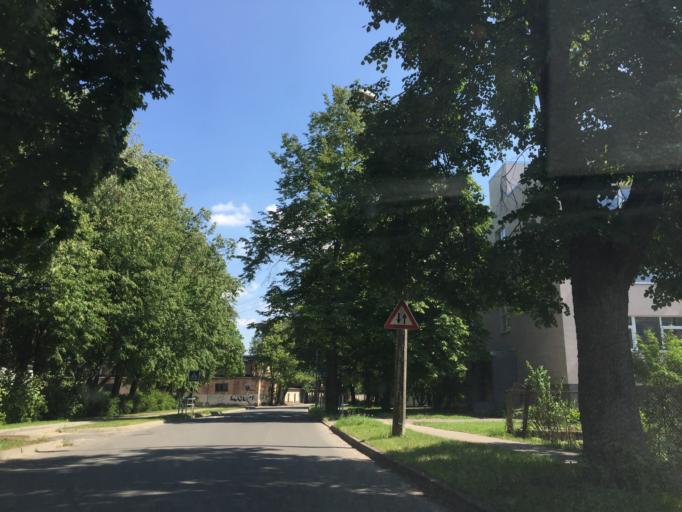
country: LV
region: Riga
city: Riga
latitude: 56.9167
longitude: 24.1032
